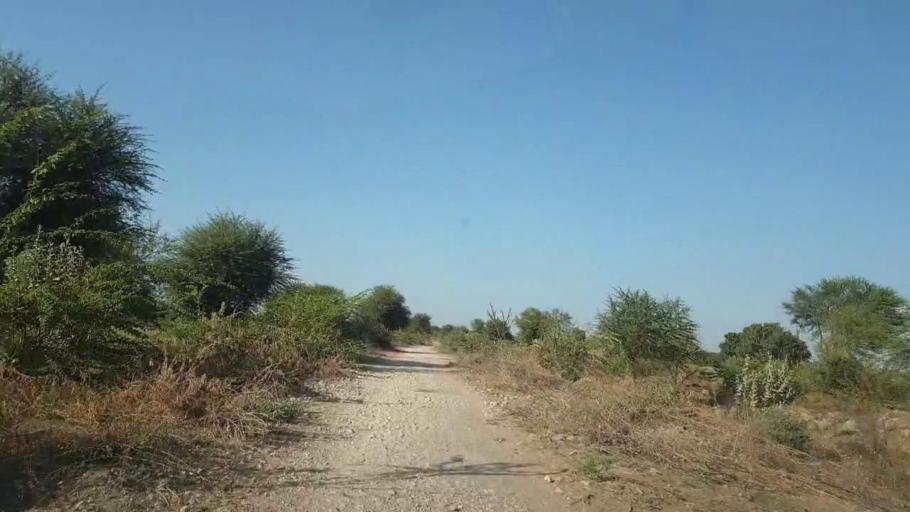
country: PK
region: Sindh
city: Kunri
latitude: 25.0593
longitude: 69.4420
